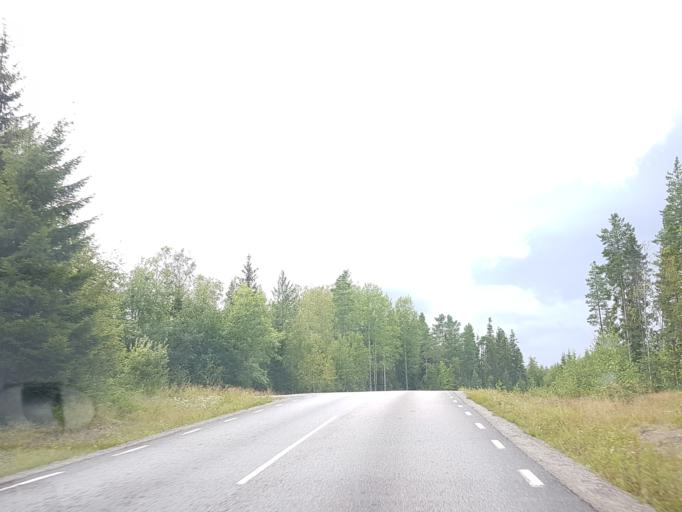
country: SE
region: Vaesterbotten
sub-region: Umea Kommun
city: Holmsund
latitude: 63.7952
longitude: 20.3702
